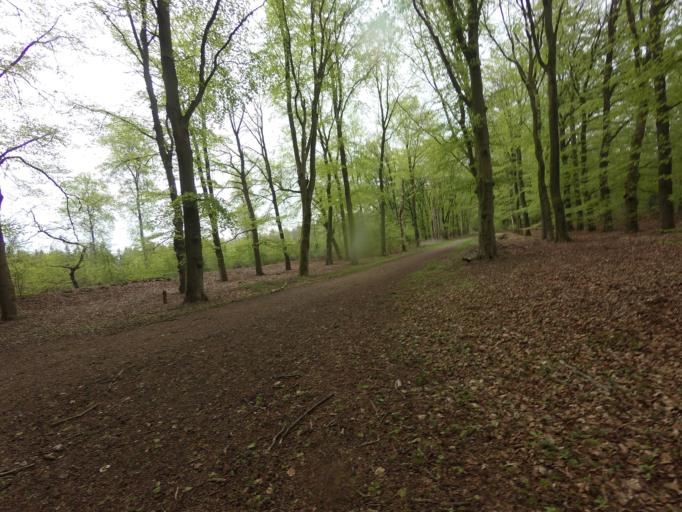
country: NL
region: Utrecht
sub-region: Gemeente Utrechtse Heuvelrug
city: Amerongen
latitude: 51.9932
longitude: 5.4835
